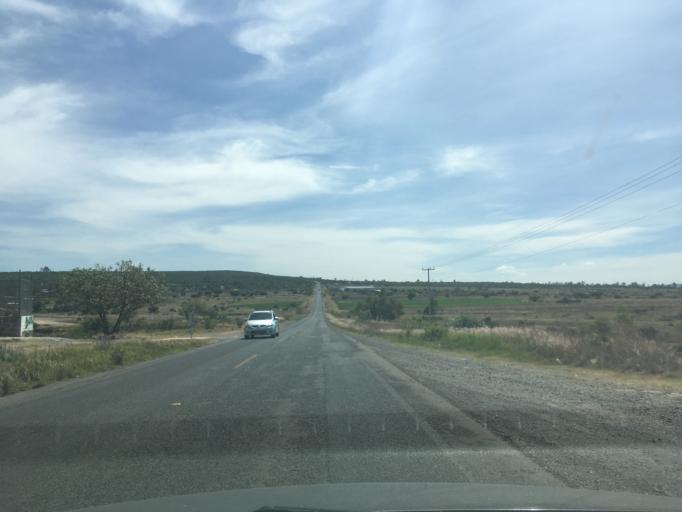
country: MX
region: Queretaro
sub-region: San Juan del Rio
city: El Jazmin
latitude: 20.3054
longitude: -100.0545
